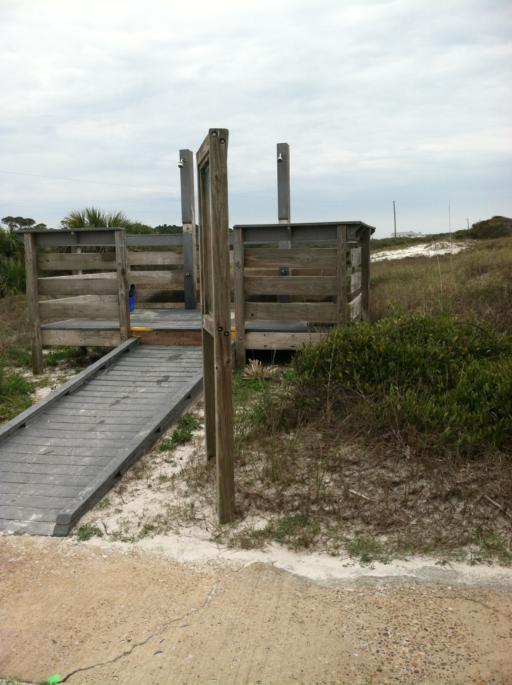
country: US
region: Florida
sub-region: Gulf County
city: Port Saint Joe
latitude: 29.7643
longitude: -85.4041
